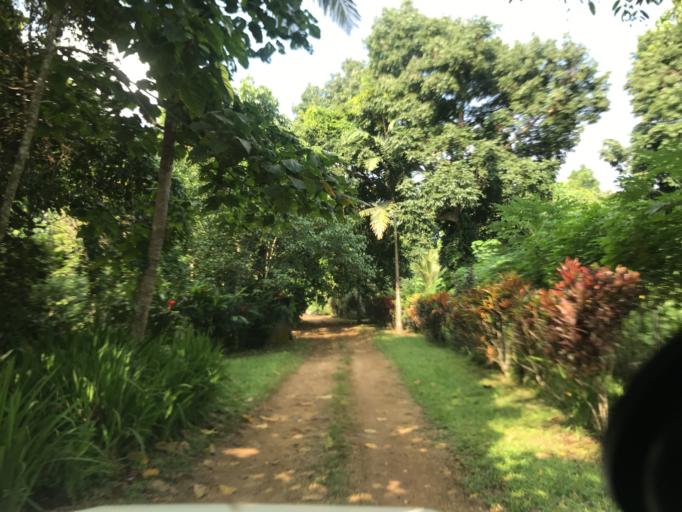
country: VU
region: Sanma
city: Luganville
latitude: -15.3130
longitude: 167.1684
